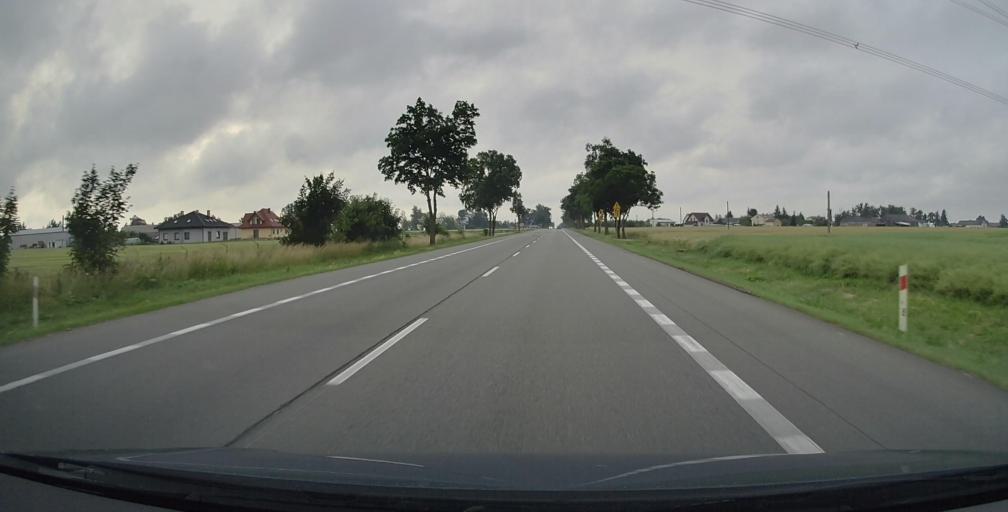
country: PL
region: Masovian Voivodeship
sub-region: Powiat siedlecki
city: Wisniew
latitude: 52.1197
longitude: 22.3589
